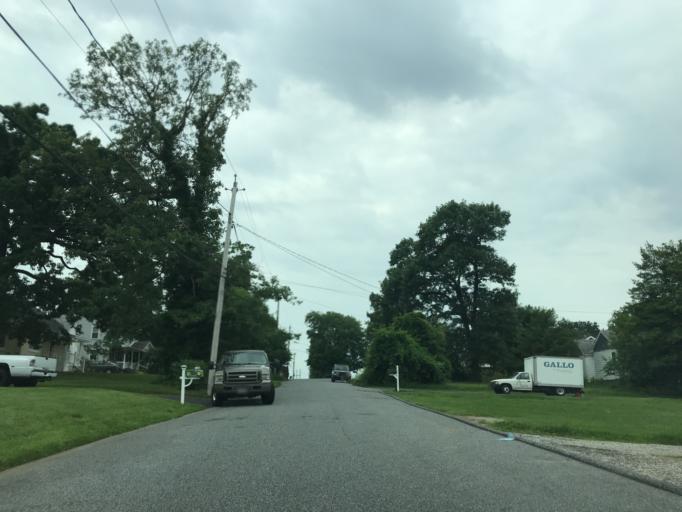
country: US
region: Maryland
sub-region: Baltimore County
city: Rossville
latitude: 39.3446
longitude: -76.5036
